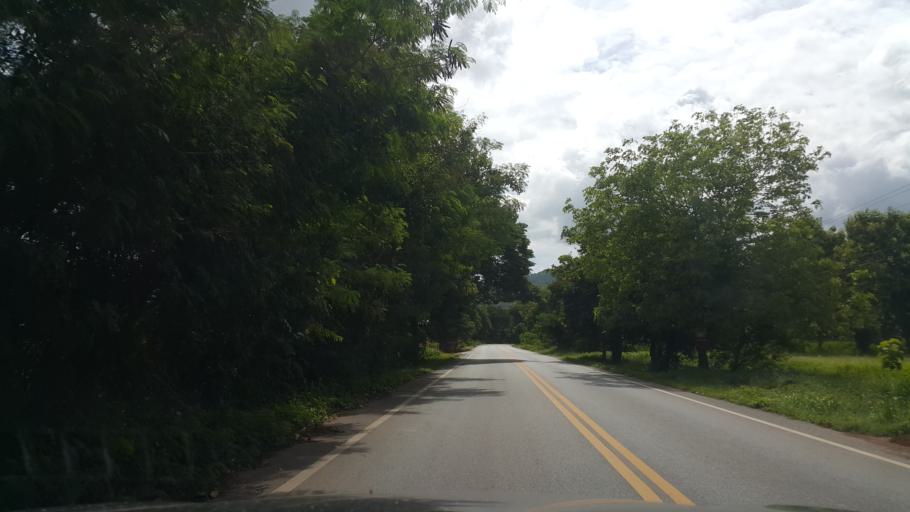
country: TH
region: Uttaradit
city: Thong Saen Khan
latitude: 17.3995
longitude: 100.3086
